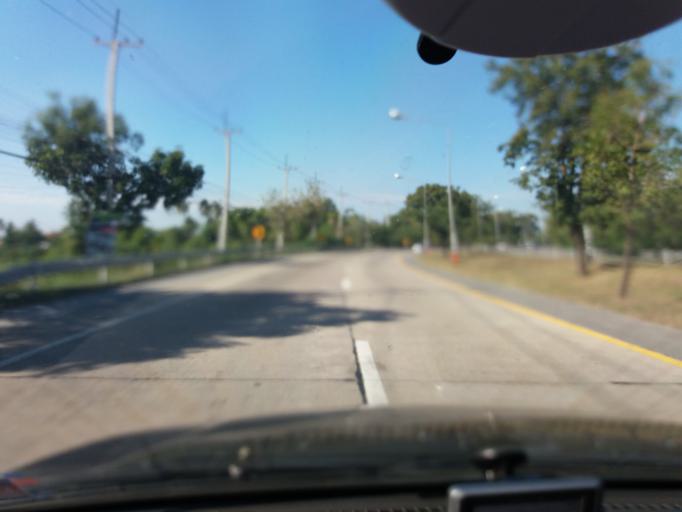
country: TH
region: Suphan Buri
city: Si Prachan
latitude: 14.5887
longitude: 100.1471
